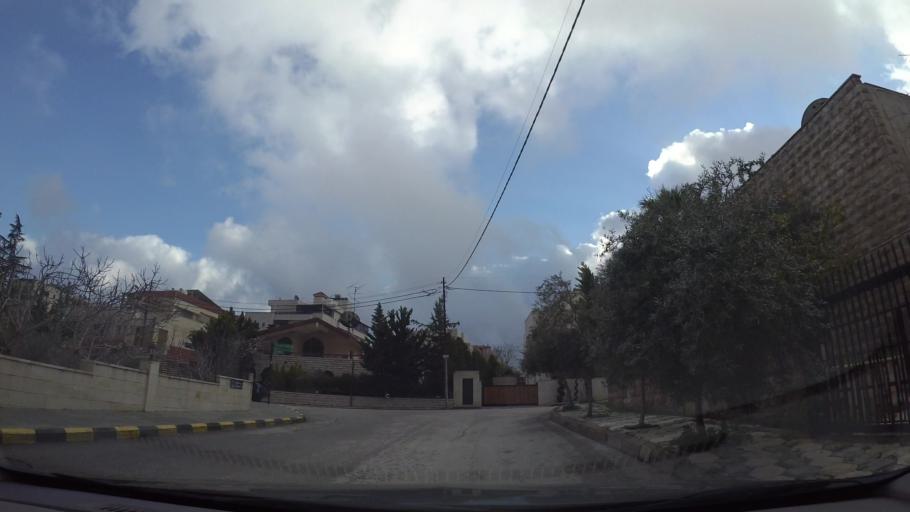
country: JO
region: Amman
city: Wadi as Sir
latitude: 31.9541
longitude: 35.8807
